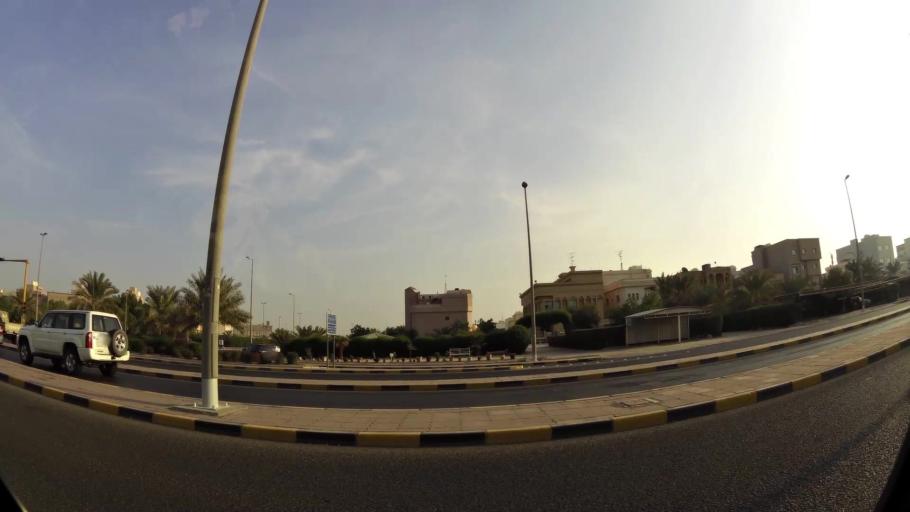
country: KW
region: Mubarak al Kabir
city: Sabah as Salim
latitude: 29.2210
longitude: 48.0608
